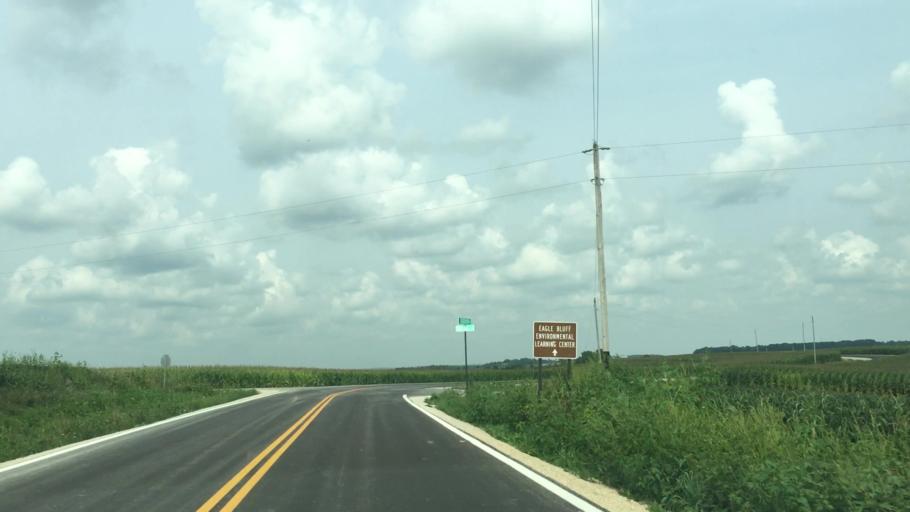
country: US
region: Minnesota
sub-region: Fillmore County
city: Preston
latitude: 43.7526
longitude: -92.0205
